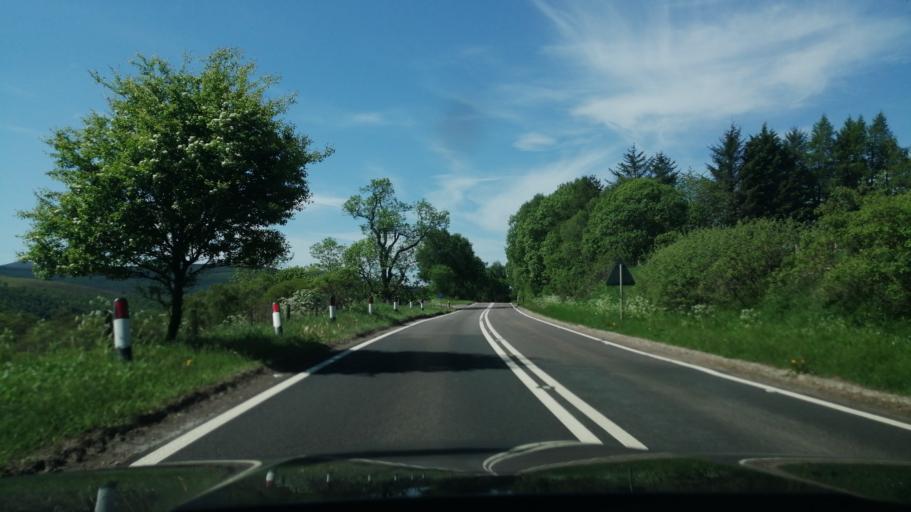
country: GB
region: Scotland
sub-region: Moray
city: Dufftown
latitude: 57.4954
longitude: -3.1474
